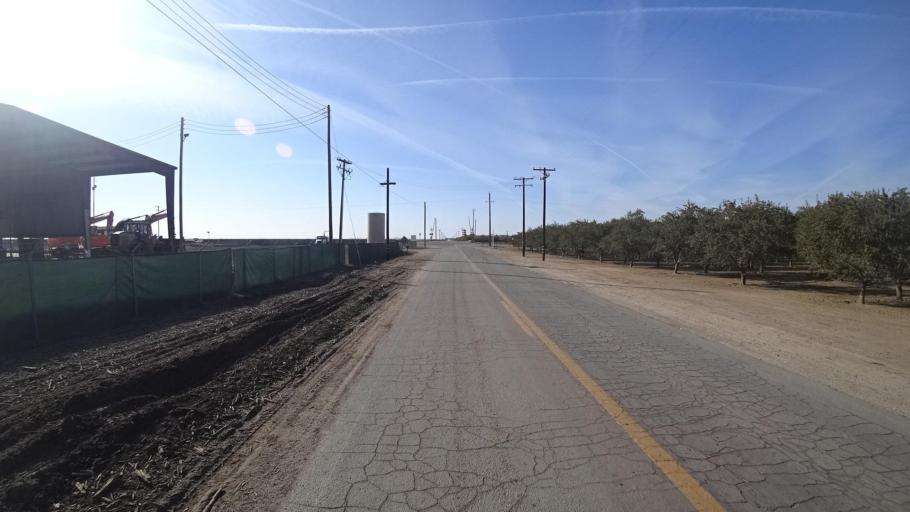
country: US
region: California
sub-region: Kern County
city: McFarland
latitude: 35.7032
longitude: -119.3294
